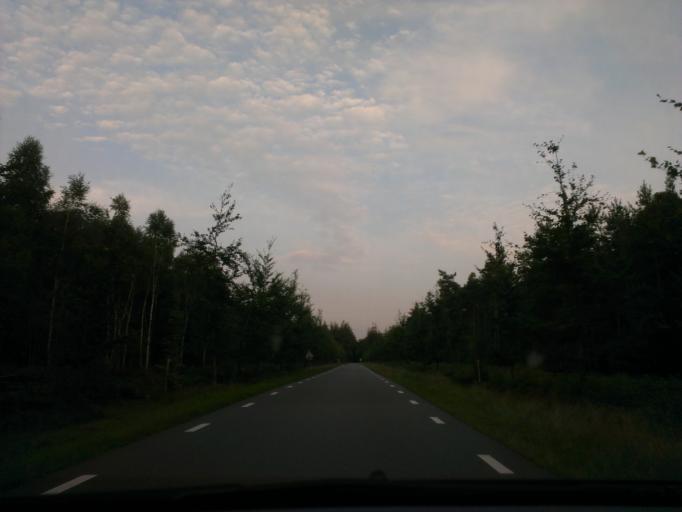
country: NL
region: Gelderland
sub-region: Gemeente Epe
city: Epe
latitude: 52.3953
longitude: 5.9730
